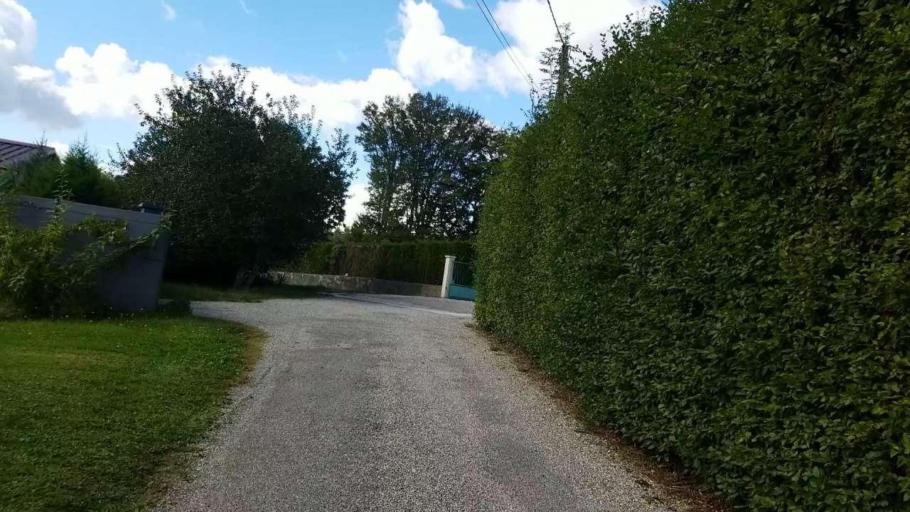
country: FR
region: Franche-Comte
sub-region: Departement du Jura
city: Chaussin
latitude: 46.8643
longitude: 5.4511
